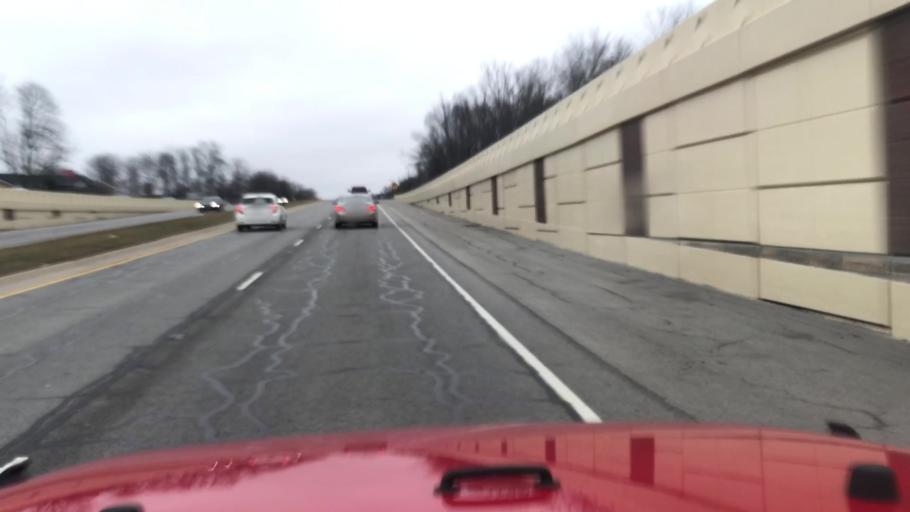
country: US
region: Indiana
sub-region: Hamilton County
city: Carmel
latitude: 39.9628
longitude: -86.1134
